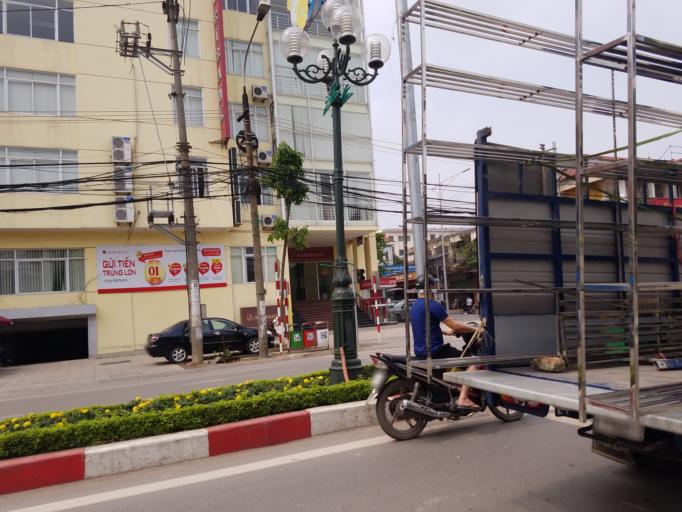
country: VN
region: Thai Nguyen
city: Thanh Pho Thai Nguyen
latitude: 21.5899
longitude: 105.8307
